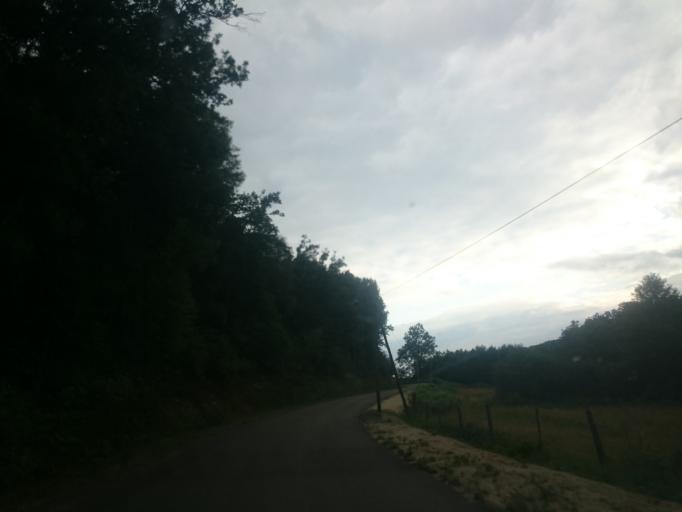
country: FR
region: Auvergne
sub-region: Departement du Cantal
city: Laroquebrou
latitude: 44.9162
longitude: 2.1931
